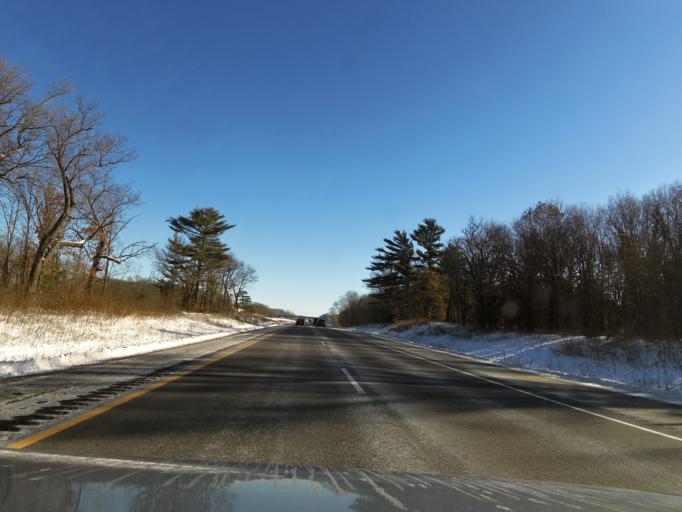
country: US
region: Wisconsin
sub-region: Juneau County
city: Mauston
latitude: 43.7687
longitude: -89.9963
